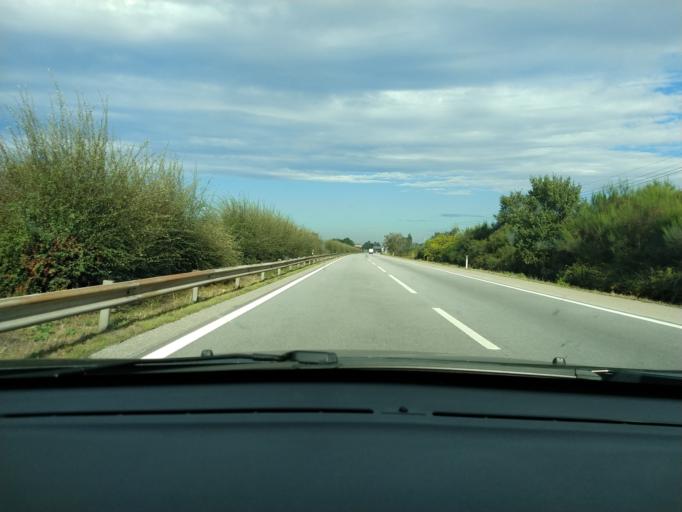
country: PT
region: Aveiro
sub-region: Estarreja
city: Salreu
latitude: 40.7494
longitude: -8.5317
